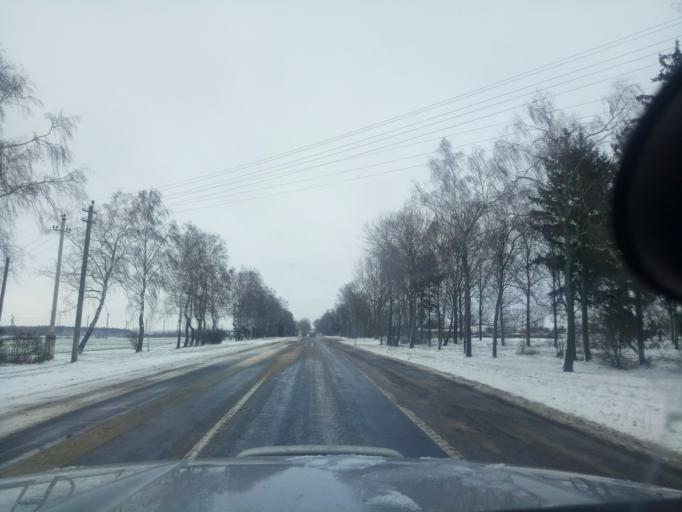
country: BY
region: Minsk
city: Tsimkavichy
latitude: 53.0880
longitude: 27.0227
